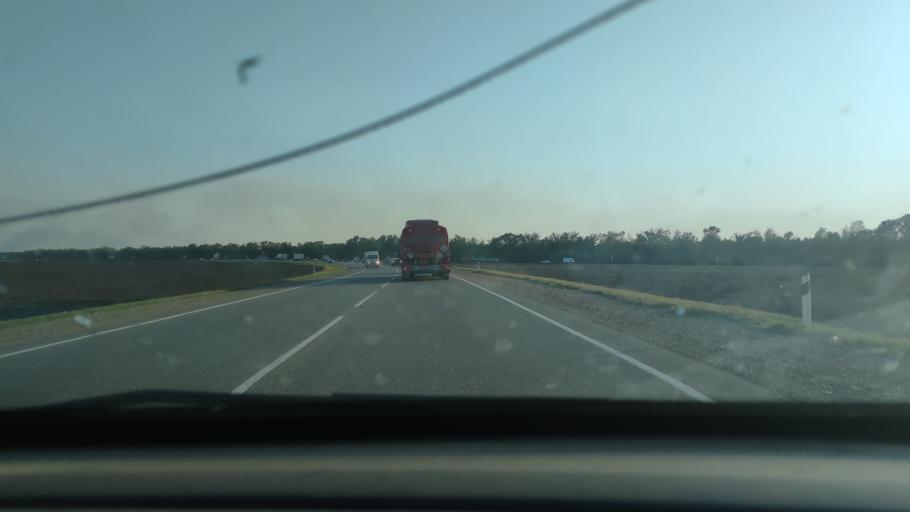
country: RU
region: Krasnodarskiy
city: Kanevskaya
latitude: 46.0288
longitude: 38.9747
